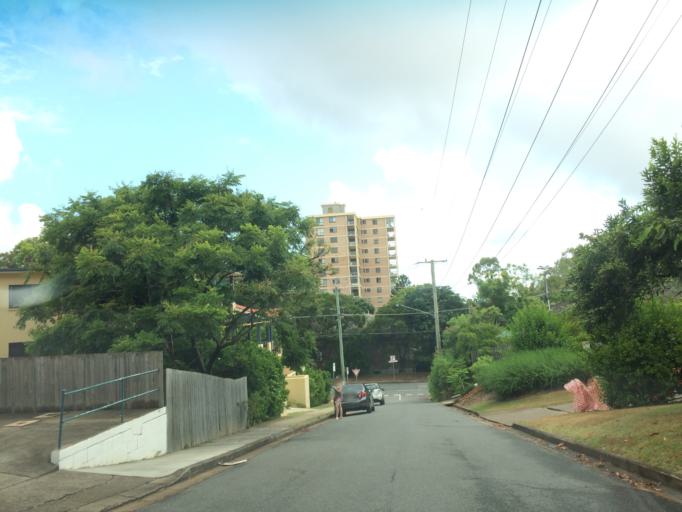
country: AU
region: Queensland
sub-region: Brisbane
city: Toowong
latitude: -27.4951
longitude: 152.9996
